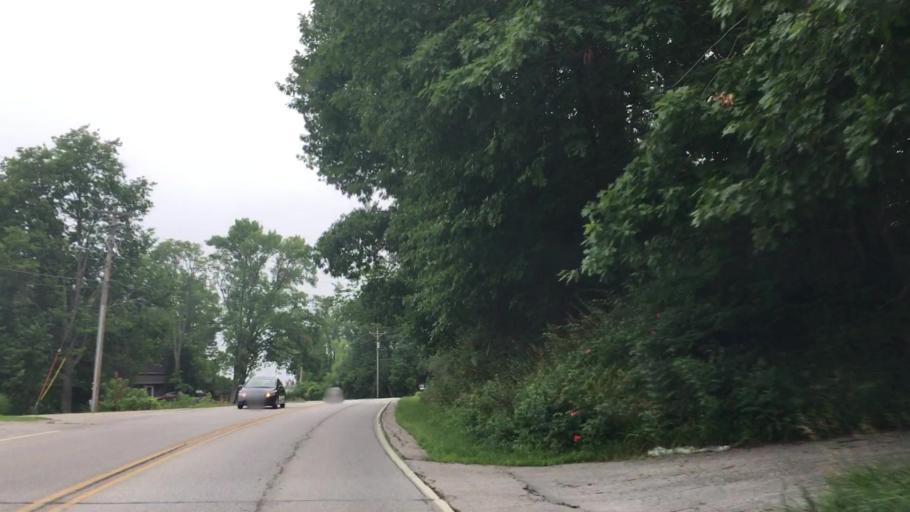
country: US
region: Iowa
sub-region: Johnson County
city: Coralville
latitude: 41.7016
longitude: -91.5455
